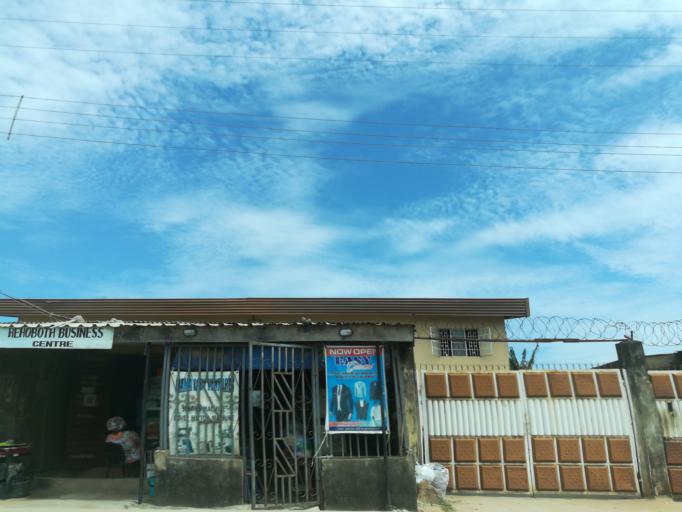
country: NG
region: Lagos
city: Ebute Ikorodu
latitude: 6.5669
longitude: 3.4786
